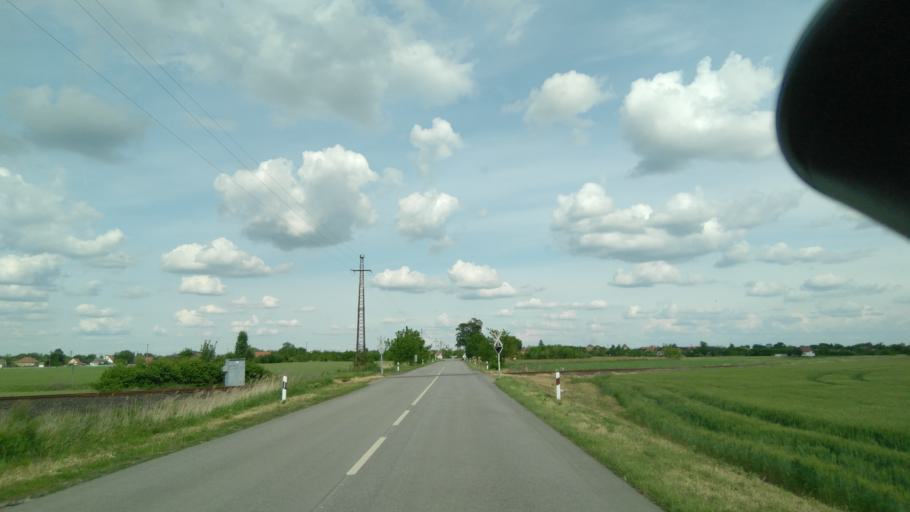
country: HU
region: Bekes
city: Battonya
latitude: 46.2916
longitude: 20.9959
